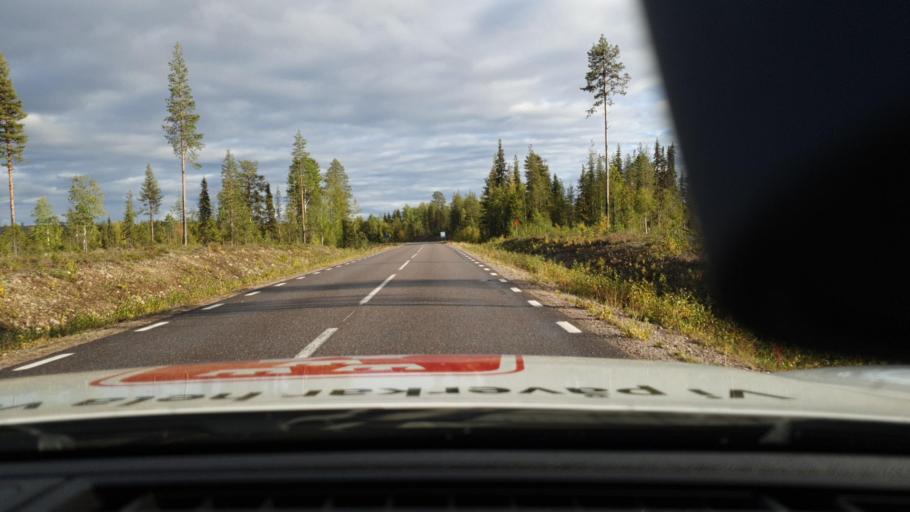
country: SE
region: Norrbotten
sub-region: Overkalix Kommun
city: OEverkalix
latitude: 66.6510
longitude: 22.6949
